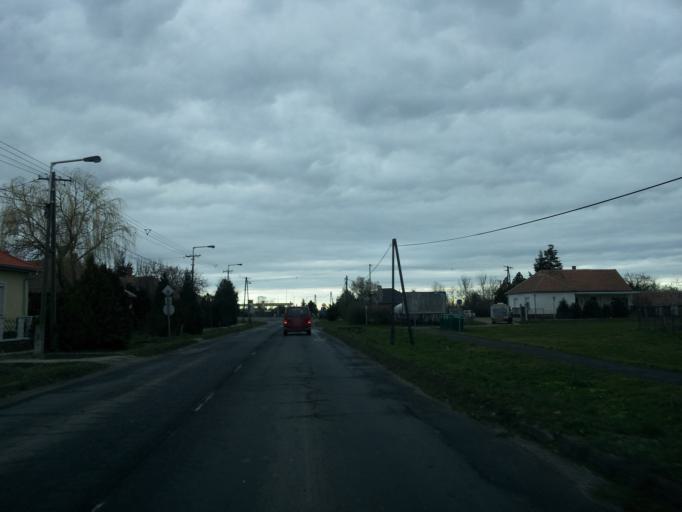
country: HU
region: Gyor-Moson-Sopron
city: Beled
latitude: 47.4748
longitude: 17.1661
